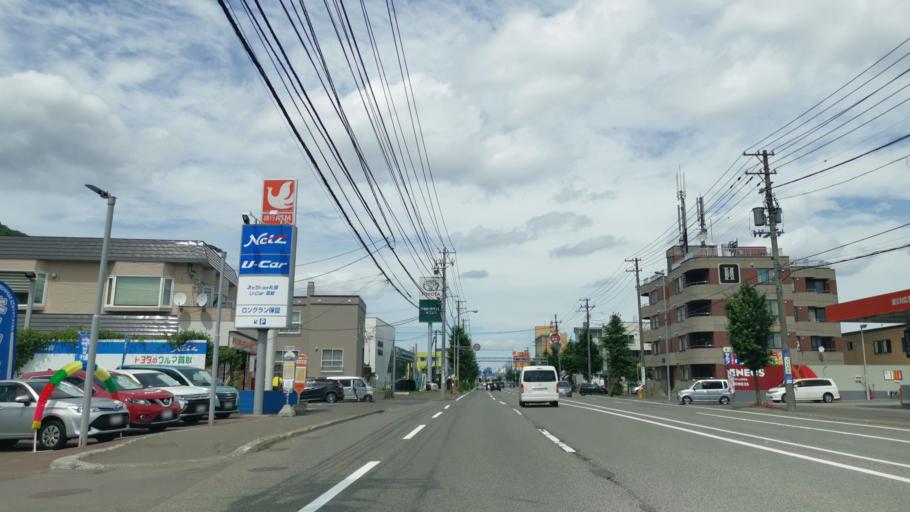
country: JP
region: Hokkaido
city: Sapporo
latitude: 43.0062
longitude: 141.3439
